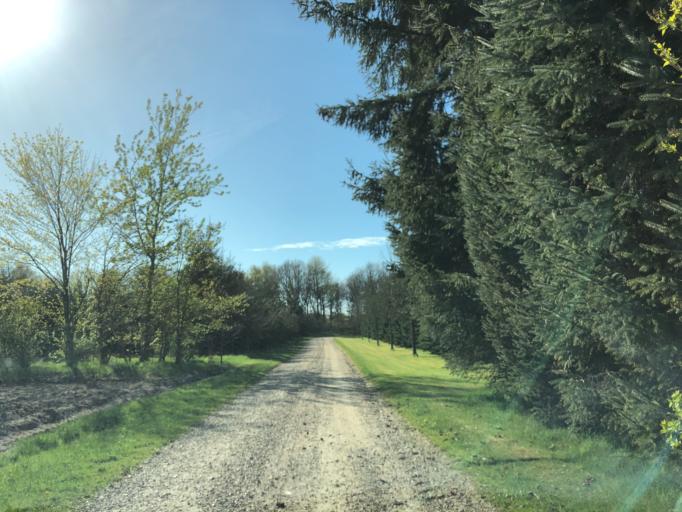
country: DK
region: Central Jutland
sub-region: Holstebro Kommune
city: Ulfborg
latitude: 56.2658
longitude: 8.3266
